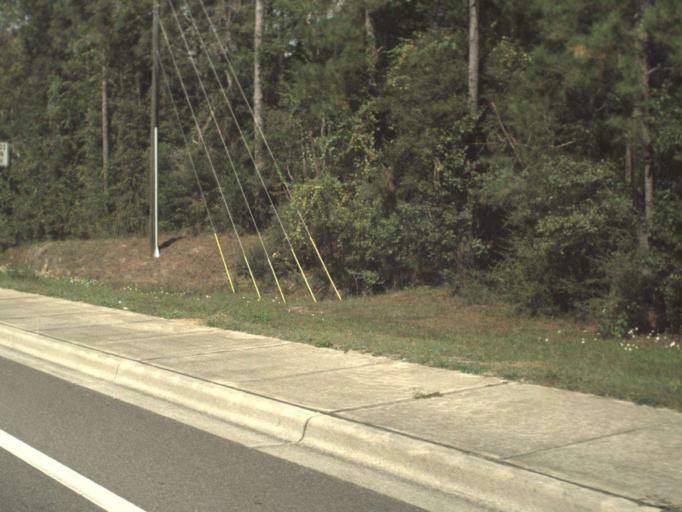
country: US
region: Florida
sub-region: Walton County
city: Freeport
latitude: 30.4900
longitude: -86.1187
